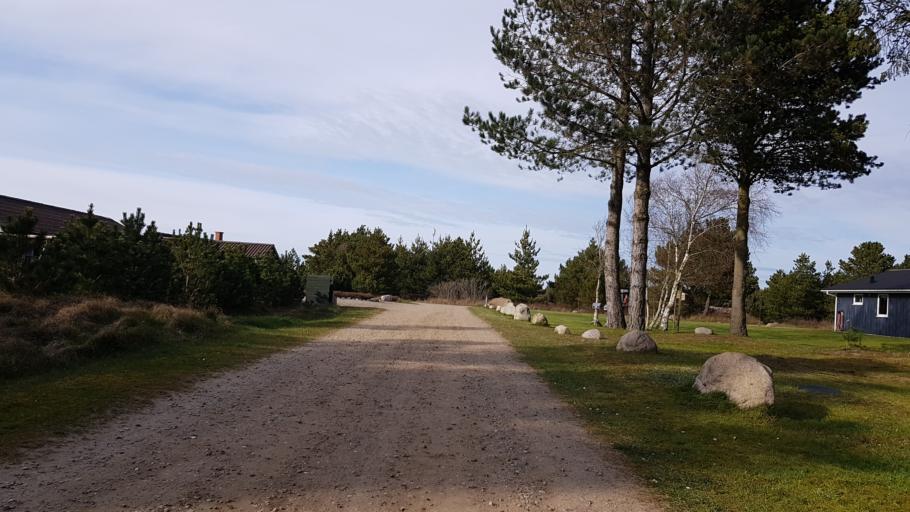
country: DE
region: Schleswig-Holstein
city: List
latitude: 55.1306
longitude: 8.5334
